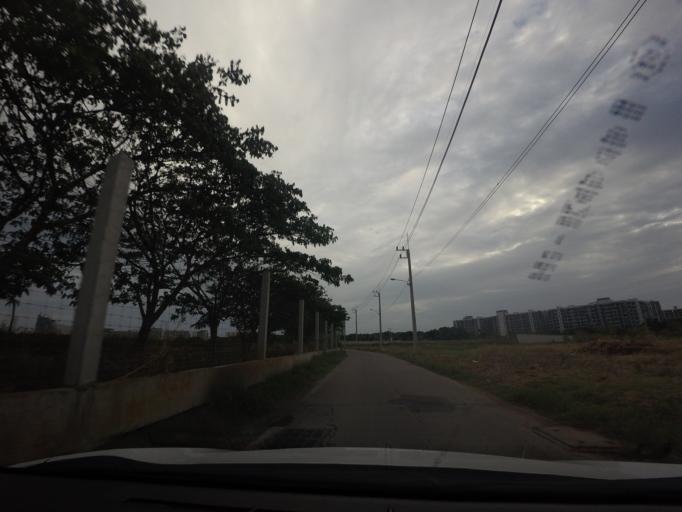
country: TH
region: Chon Buri
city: Phatthaya
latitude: 12.9012
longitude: 100.8843
